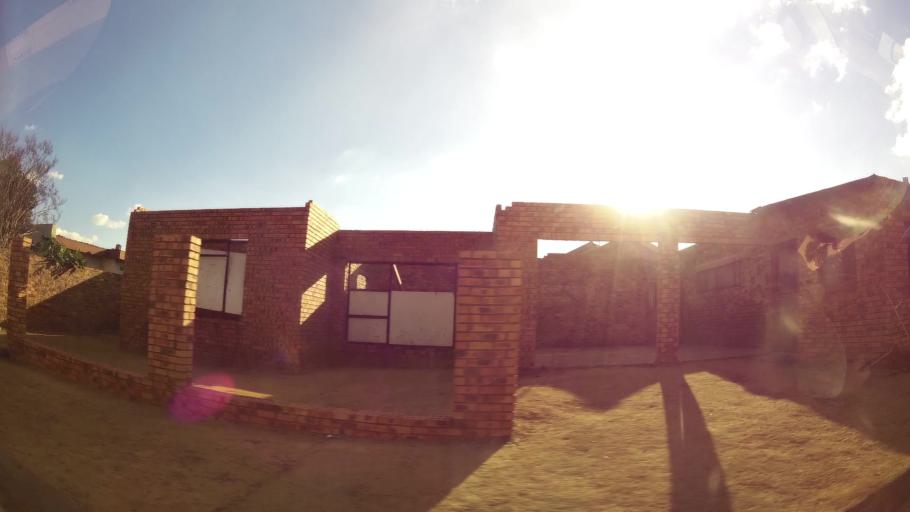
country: ZA
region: Mpumalanga
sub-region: Nkangala District Municipality
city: Witbank
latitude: -25.8704
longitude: 29.1817
